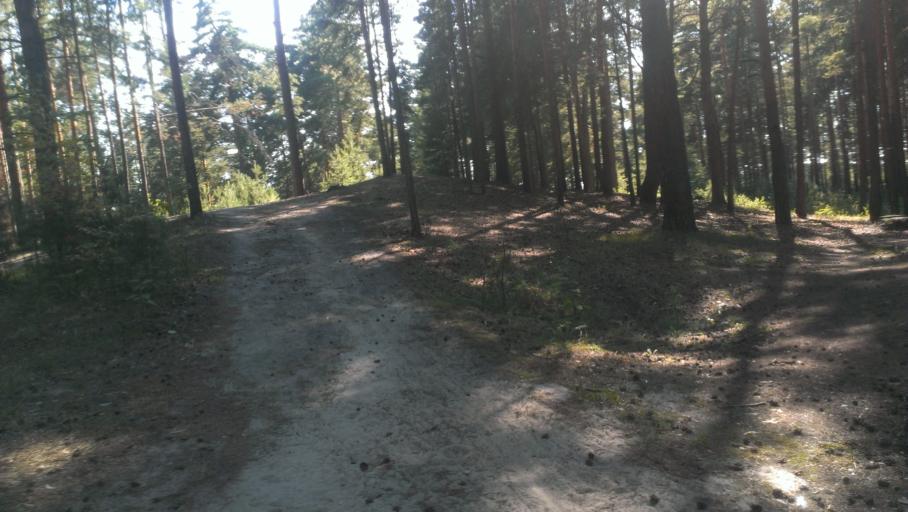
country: RU
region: Altai Krai
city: Novosilikatnyy
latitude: 53.3169
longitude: 83.6790
